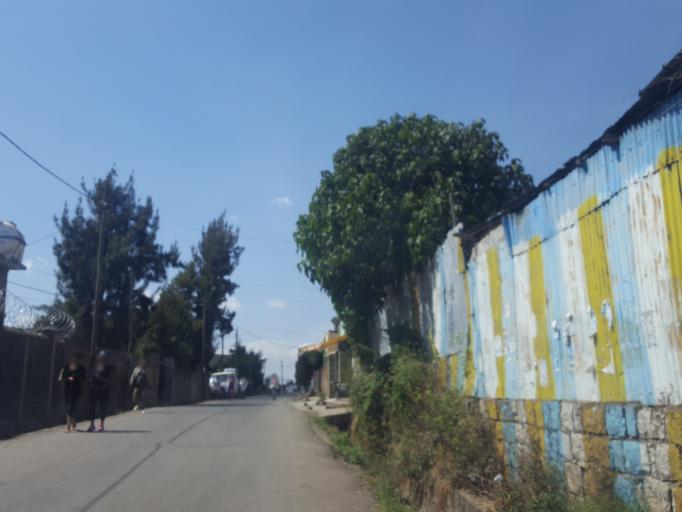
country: ET
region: Adis Abeba
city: Addis Ababa
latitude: 9.0611
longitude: 38.7349
